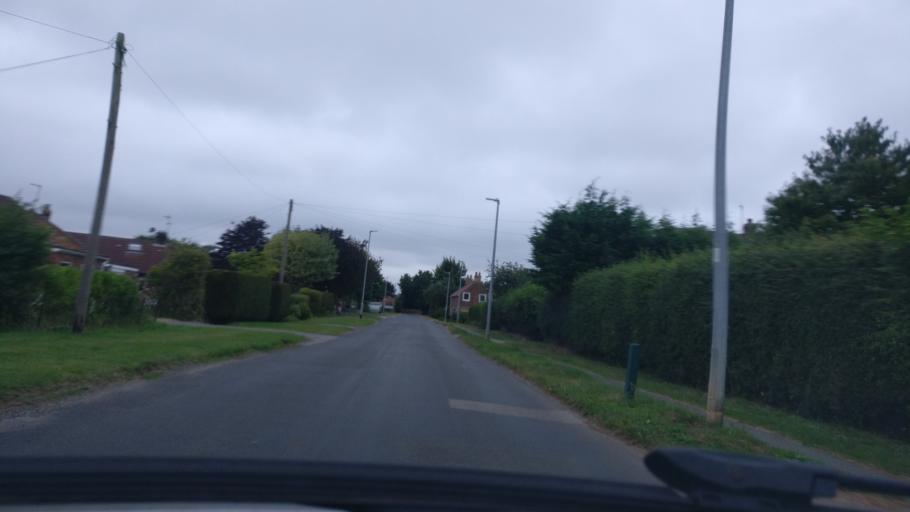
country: GB
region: England
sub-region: East Riding of Yorkshire
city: Leven
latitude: 53.8928
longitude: -0.3235
